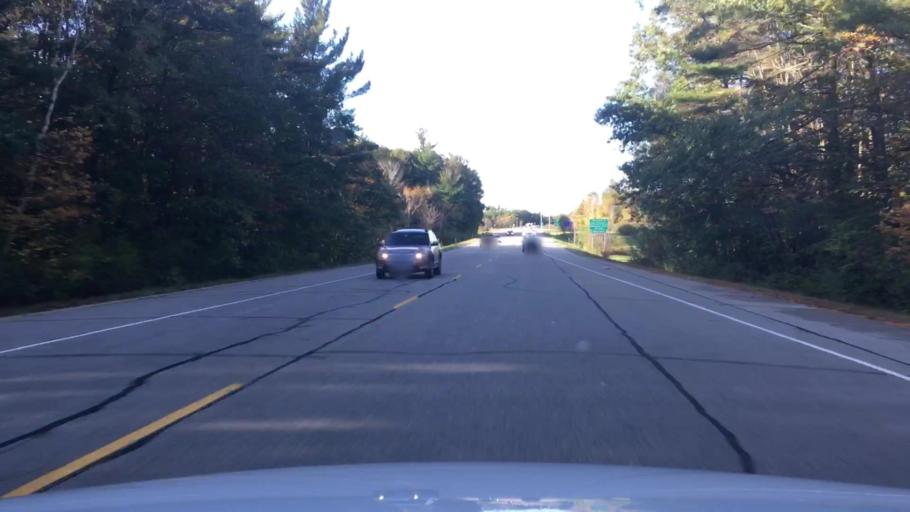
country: US
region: New Hampshire
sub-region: Strafford County
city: Durham
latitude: 43.1506
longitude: -70.9494
